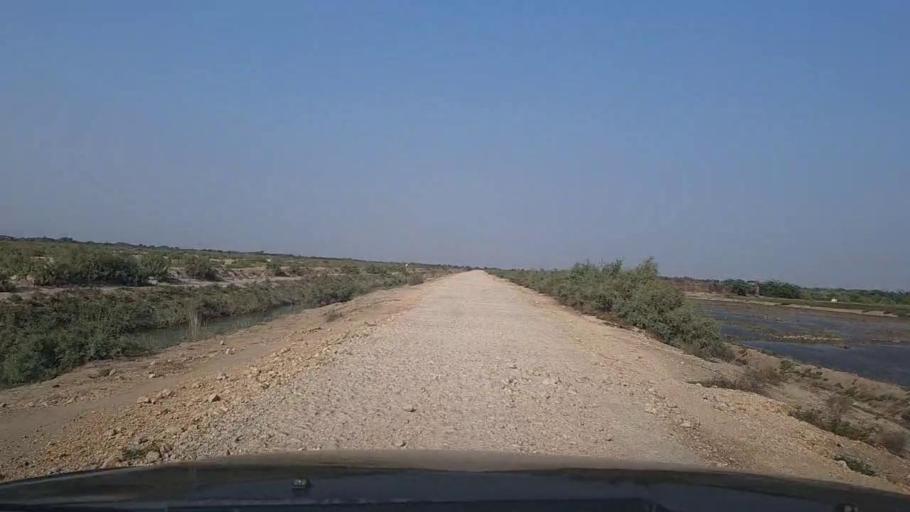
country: PK
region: Sindh
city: Mirpur Sakro
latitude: 24.6453
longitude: 67.7535
